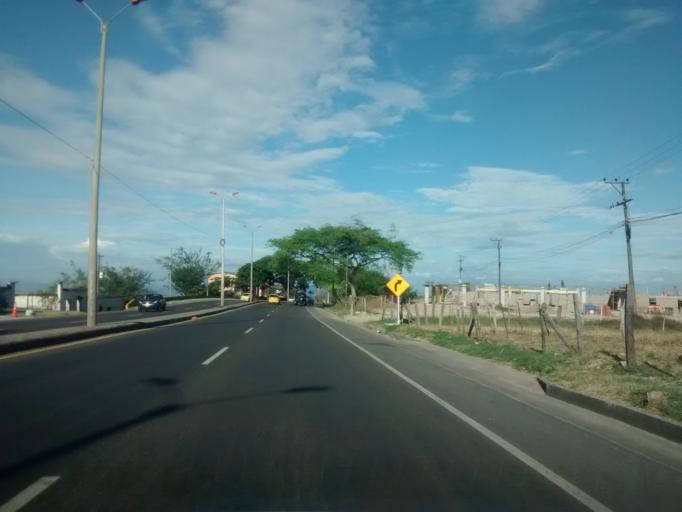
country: CO
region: Tolima
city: Ibague
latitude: 4.4199
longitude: -75.1811
